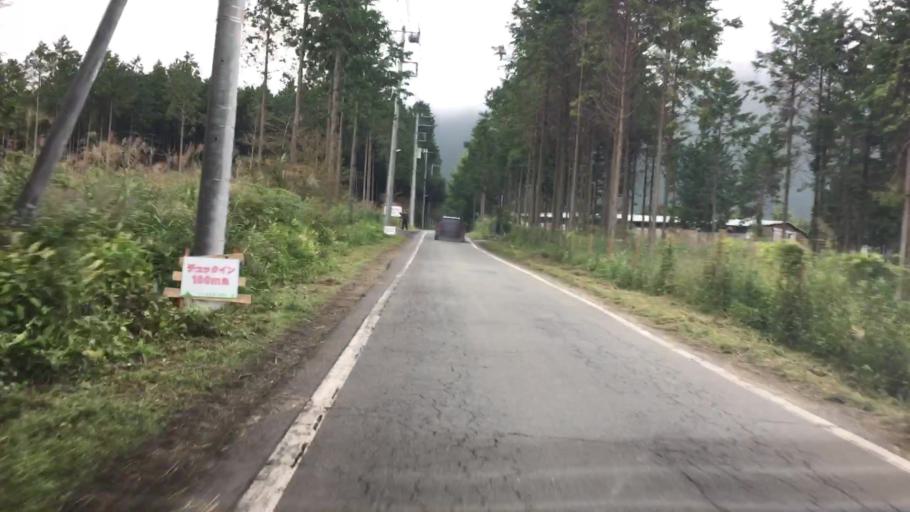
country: JP
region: Yamanashi
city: Fujikawaguchiko
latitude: 35.3968
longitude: 138.5654
